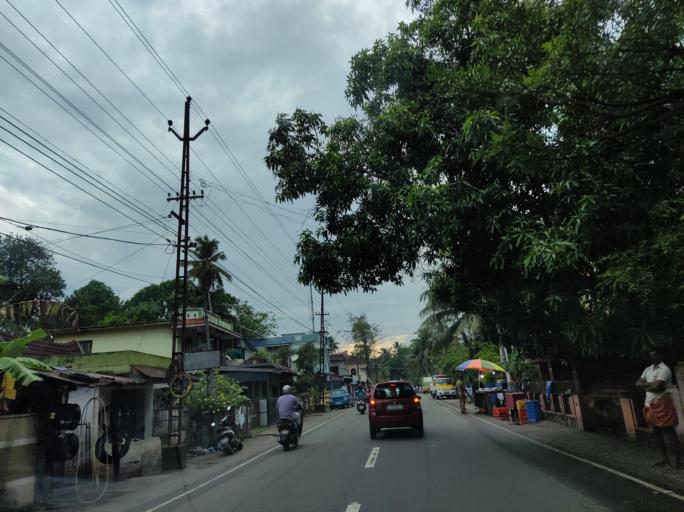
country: IN
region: Kerala
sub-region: Alappuzha
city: Mavelikara
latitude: 9.2518
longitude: 76.4868
